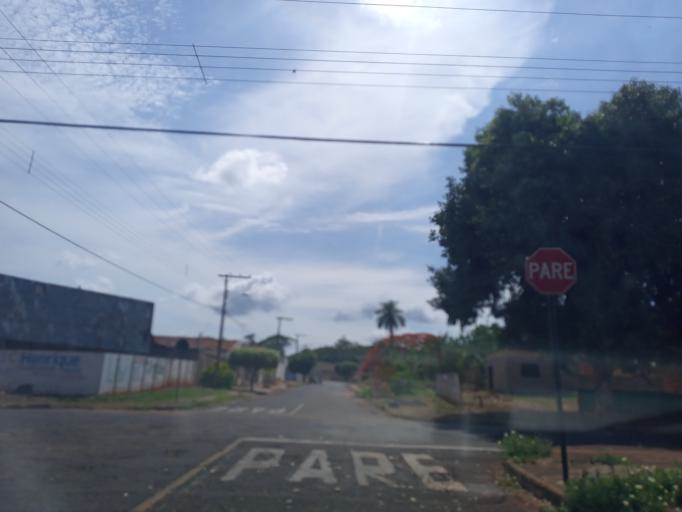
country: BR
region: Minas Gerais
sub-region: Ituiutaba
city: Ituiutaba
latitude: -18.9887
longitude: -49.4701
